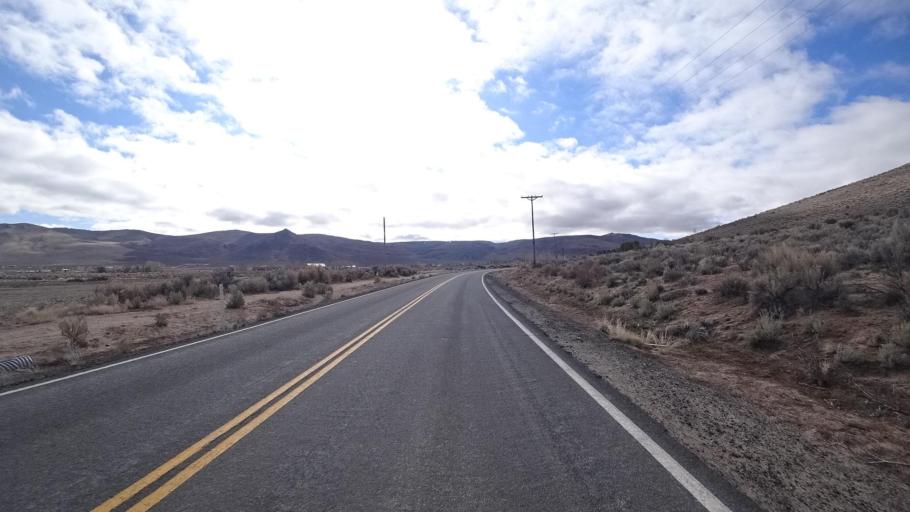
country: US
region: Nevada
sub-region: Washoe County
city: Cold Springs
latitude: 39.8608
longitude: -119.9367
